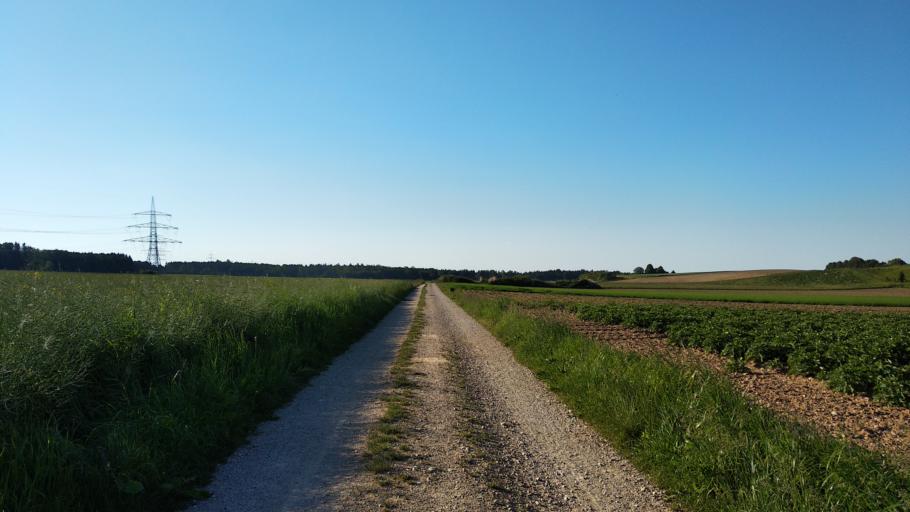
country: DE
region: Bavaria
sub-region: Upper Bavaria
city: Zorneding
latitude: 48.0969
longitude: 11.8195
